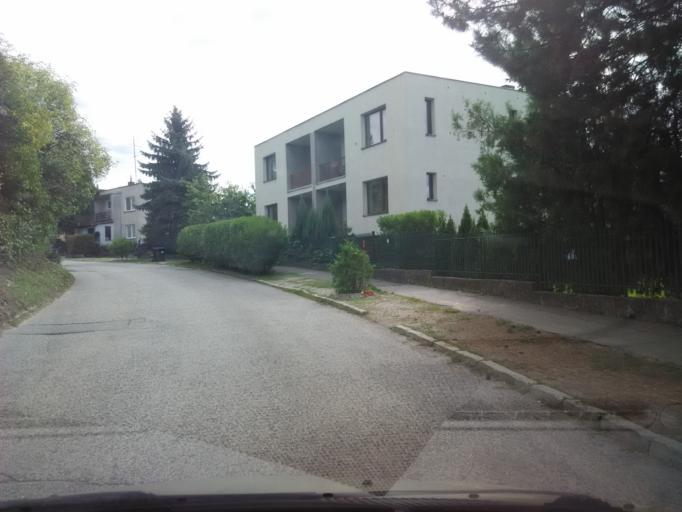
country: SK
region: Nitriansky
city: Levice
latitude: 48.2139
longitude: 18.6202
